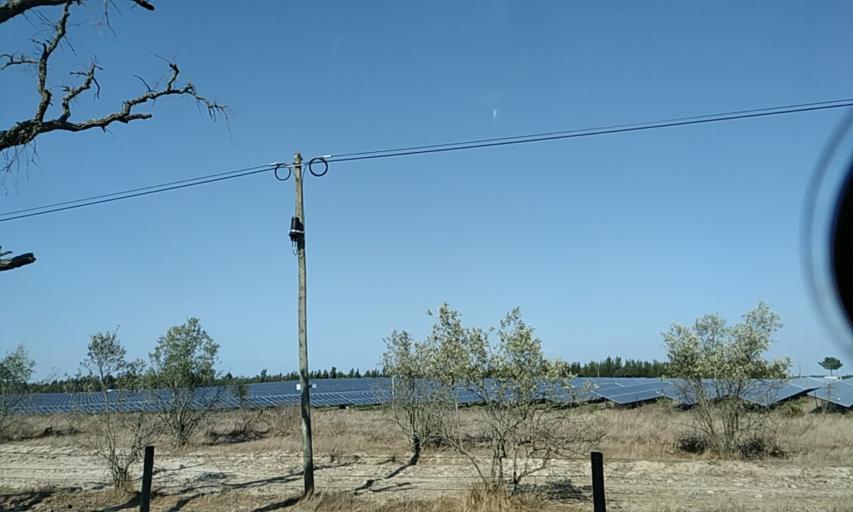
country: PT
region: Evora
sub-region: Vendas Novas
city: Vendas Novas
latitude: 38.7250
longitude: -8.6211
